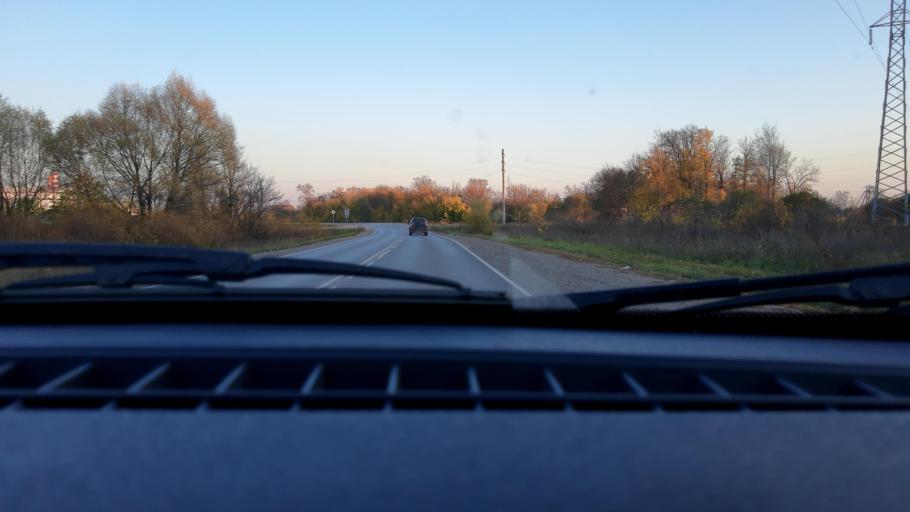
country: RU
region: Bashkortostan
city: Mikhaylovka
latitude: 54.8057
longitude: 55.8230
